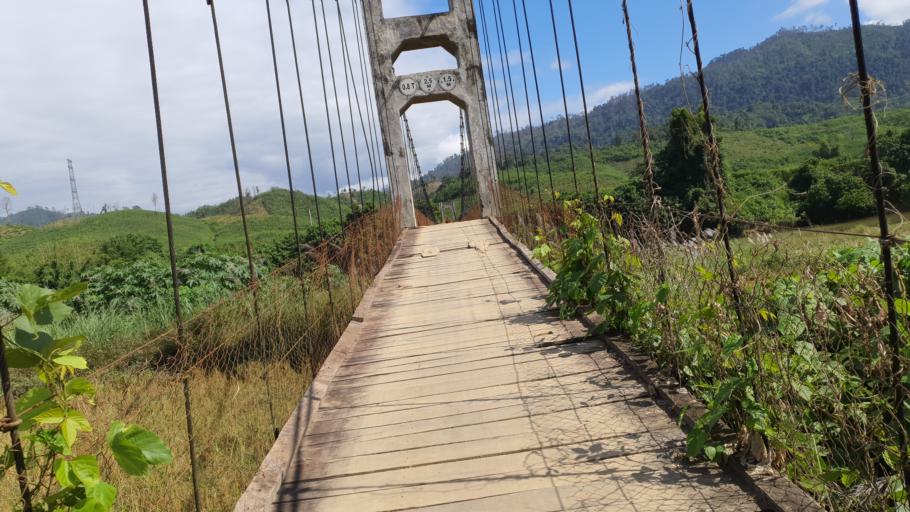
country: LA
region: Bolikhamxai
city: Bolikhan
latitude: 18.9090
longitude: 103.7423
